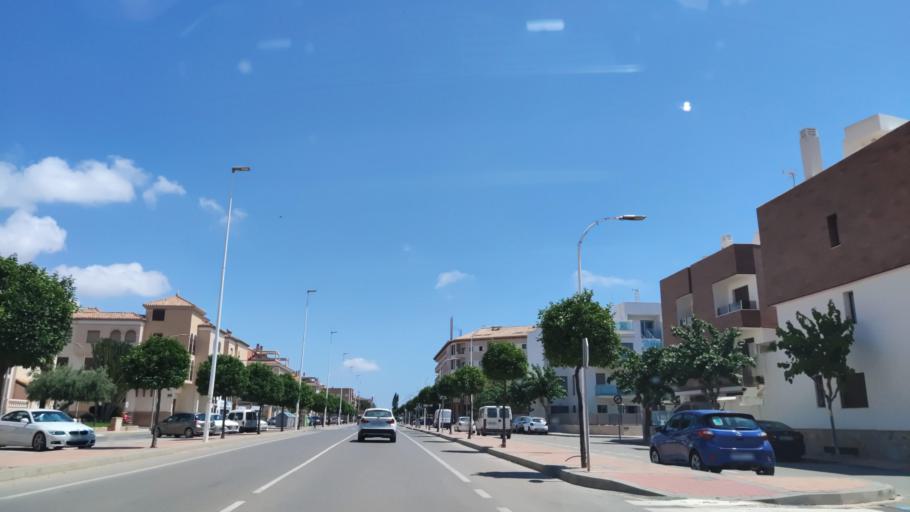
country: ES
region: Murcia
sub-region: Murcia
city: Los Alcazares
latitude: 37.7534
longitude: -0.8431
